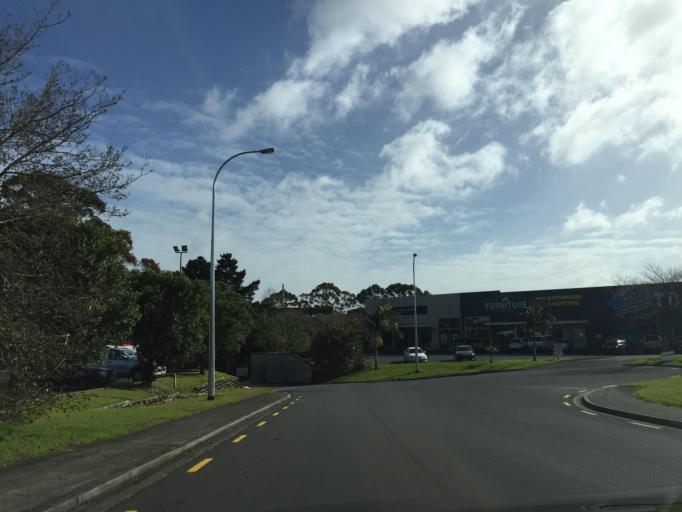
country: NZ
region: Auckland
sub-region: Auckland
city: Rothesay Bay
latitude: -36.7490
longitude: 174.7277
